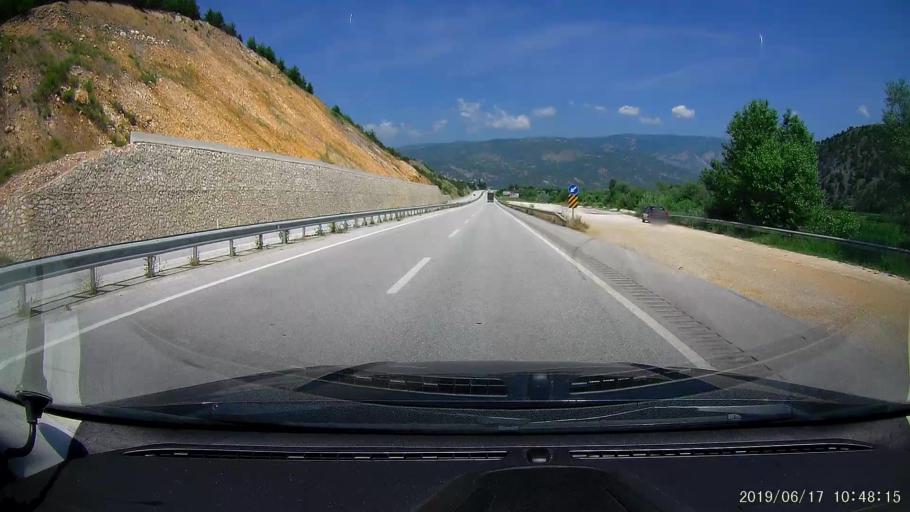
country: TR
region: Corum
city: Hacihamza
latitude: 41.0850
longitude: 34.4327
